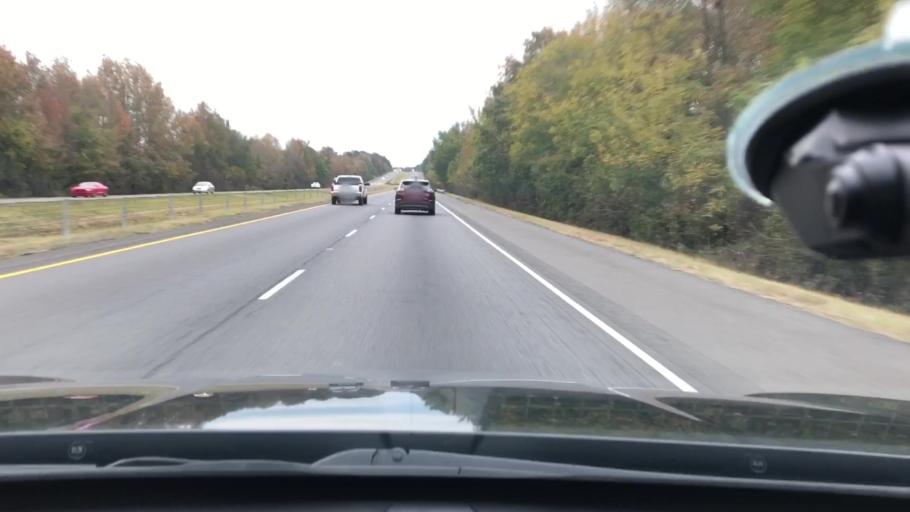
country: US
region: Arkansas
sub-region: Clark County
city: Gurdon
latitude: 34.0238
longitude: -93.1559
